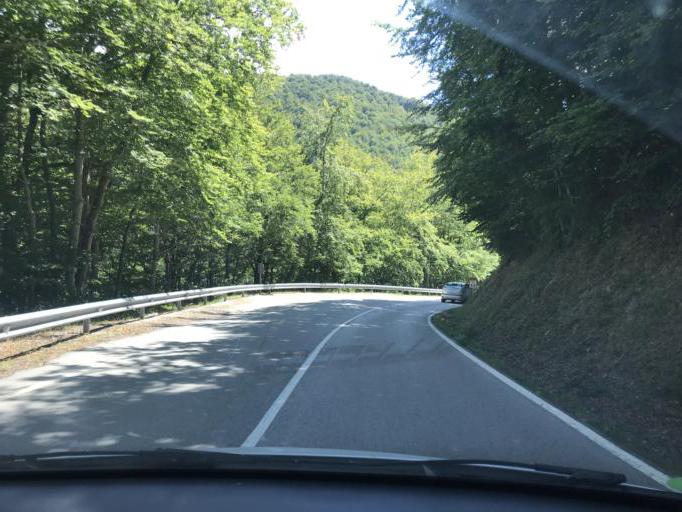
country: ES
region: Cantabria
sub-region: Provincia de Cantabria
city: Cabezon de Liebana
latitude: 43.0683
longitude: -4.4788
